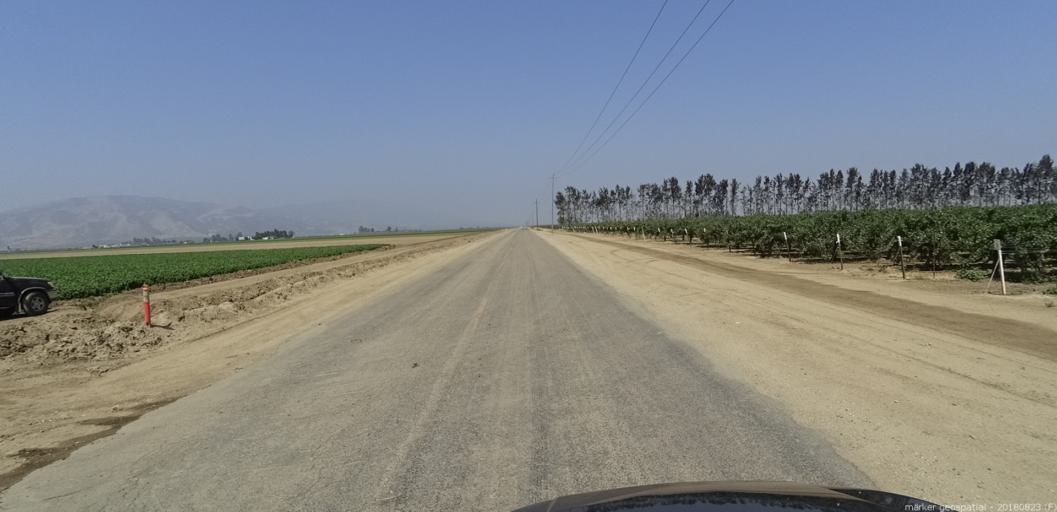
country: US
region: California
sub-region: Monterey County
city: Greenfield
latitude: 36.2923
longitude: -121.2549
